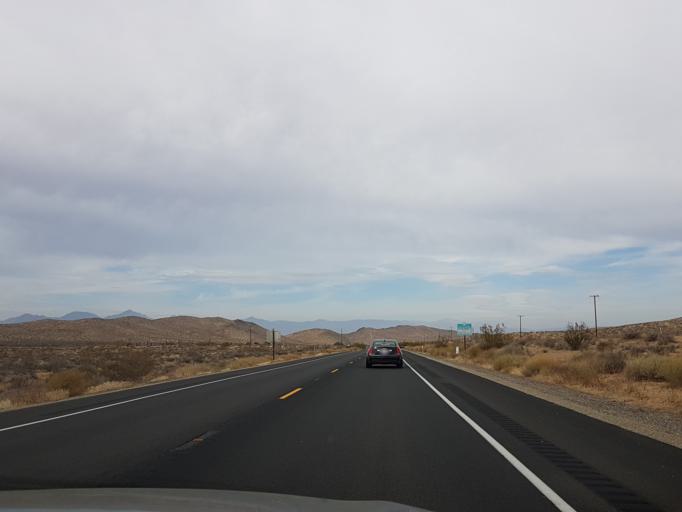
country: US
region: California
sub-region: Kern County
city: Ridgecrest
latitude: 35.5241
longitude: -117.6755
